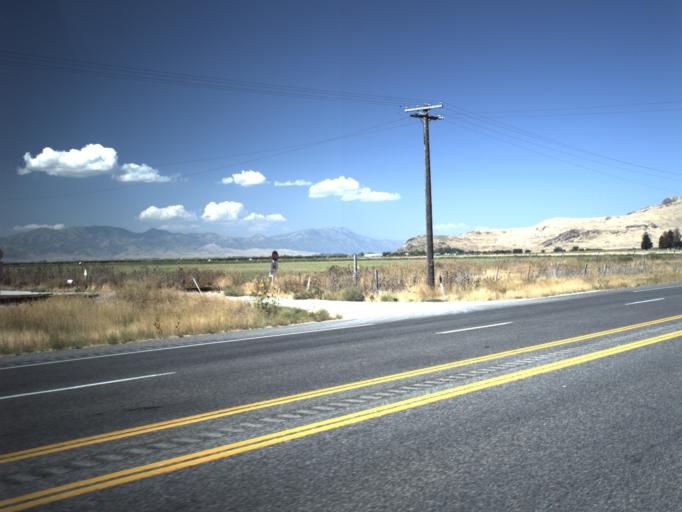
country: US
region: Utah
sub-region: Cache County
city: Lewiston
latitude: 41.9938
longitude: -111.8127
